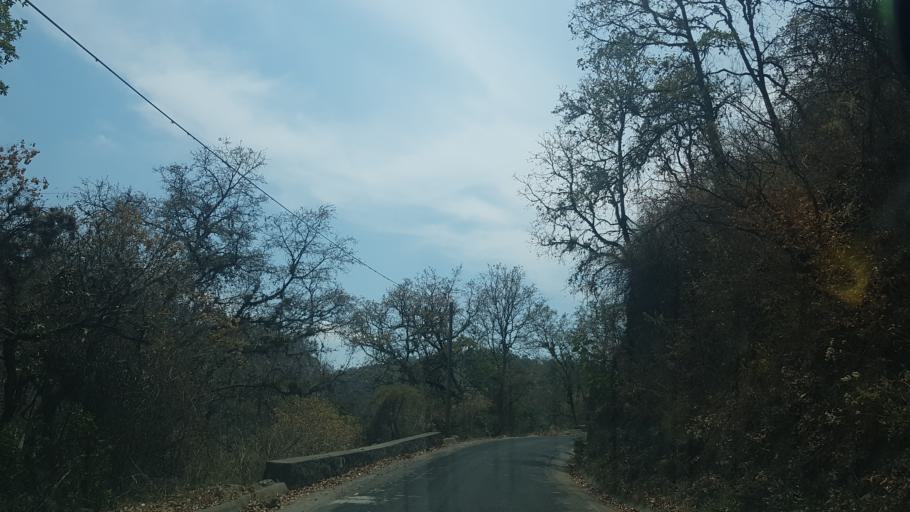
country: MX
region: Puebla
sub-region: Tochimilco
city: La Magdalena Yancuitlalpan
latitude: 18.8747
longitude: -98.6116
